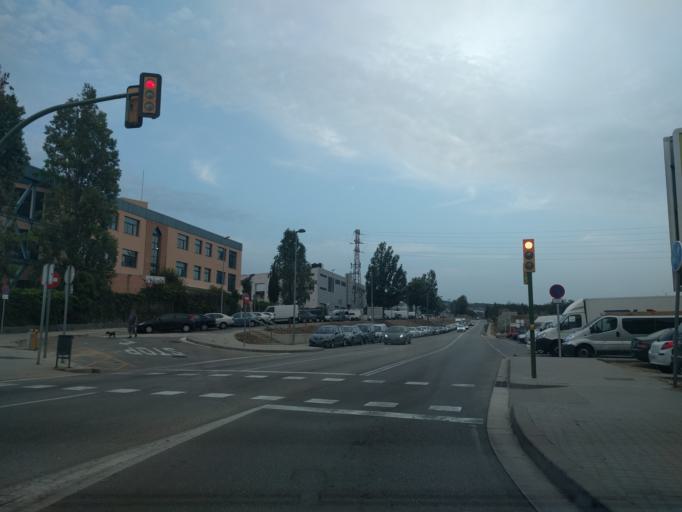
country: ES
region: Catalonia
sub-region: Provincia de Barcelona
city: Mataro
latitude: 41.5490
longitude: 2.4531
